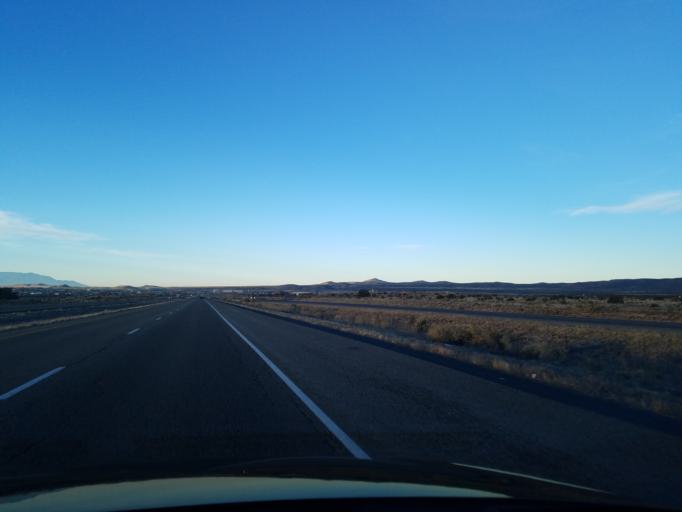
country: US
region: New Mexico
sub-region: Santa Fe County
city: Agua Fria
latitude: 35.6485
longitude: -106.0533
